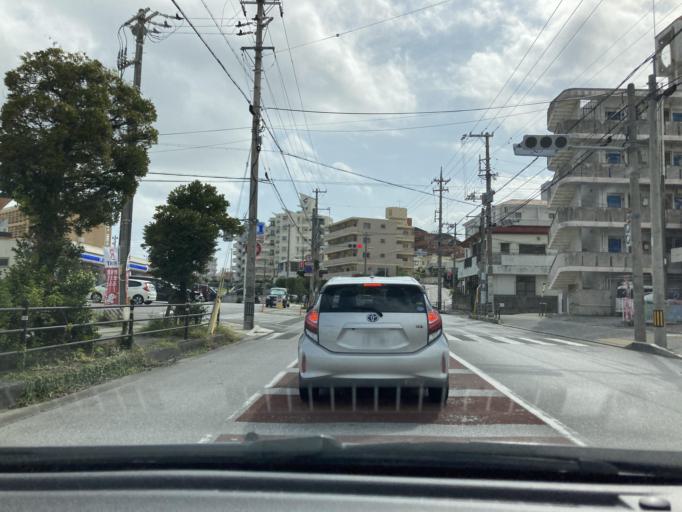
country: JP
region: Okinawa
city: Ginowan
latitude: 26.2616
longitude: 127.7519
